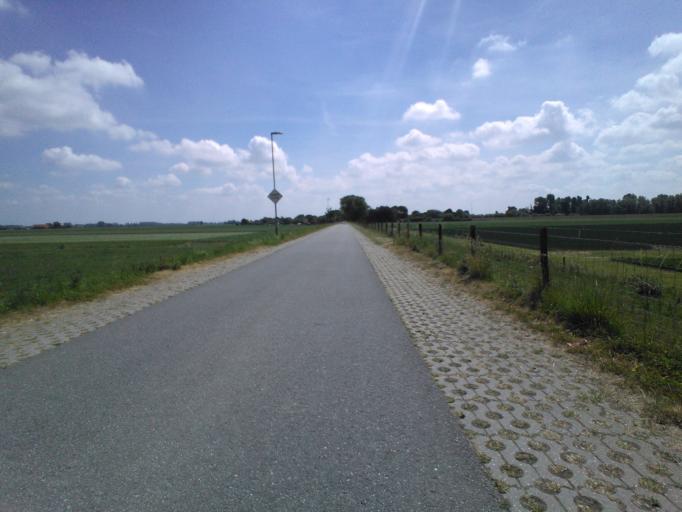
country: NL
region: North Brabant
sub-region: Gemeente Geertruidenberg
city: Geertruidenberg
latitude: 51.7242
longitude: 4.9007
